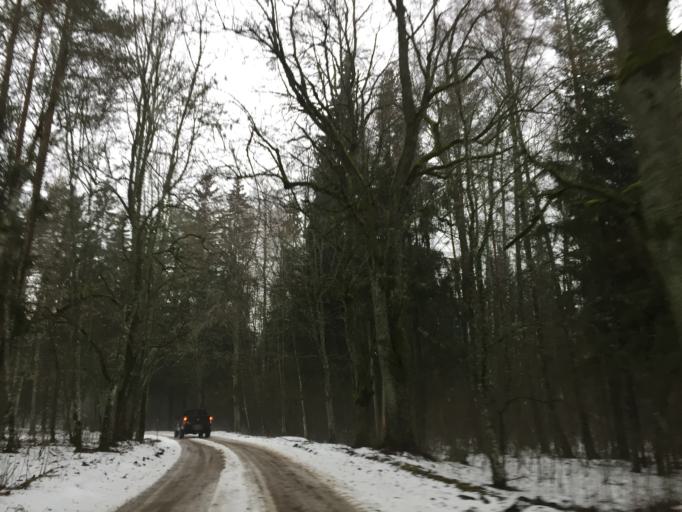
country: LV
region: Incukalns
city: Vangazi
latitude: 57.1257
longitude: 24.5710
